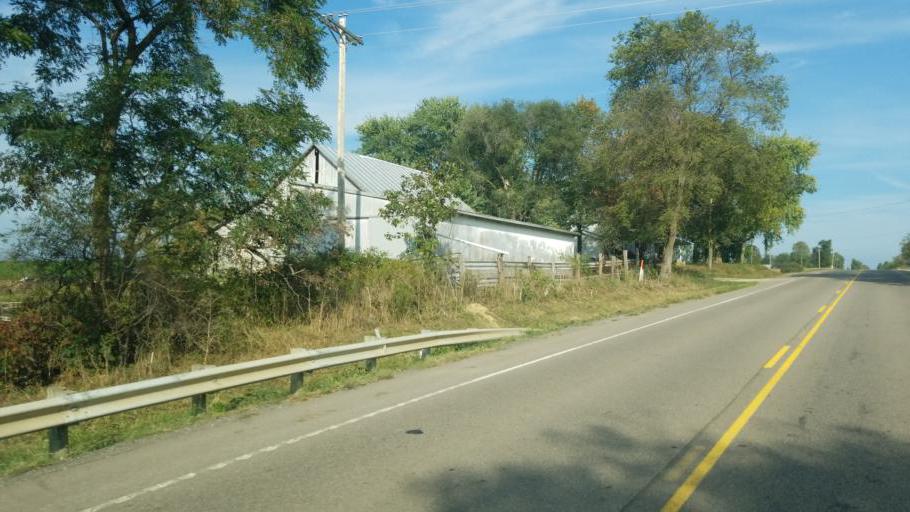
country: US
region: Ohio
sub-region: Licking County
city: Utica
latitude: 40.2705
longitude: -82.3712
